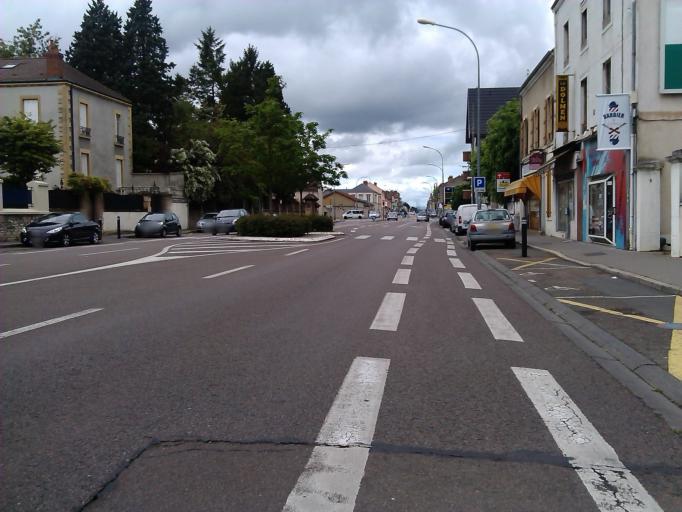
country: FR
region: Bourgogne
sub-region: Departement de Saone-et-Loire
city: Chalon-sur-Saone
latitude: 46.7906
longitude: 4.8501
